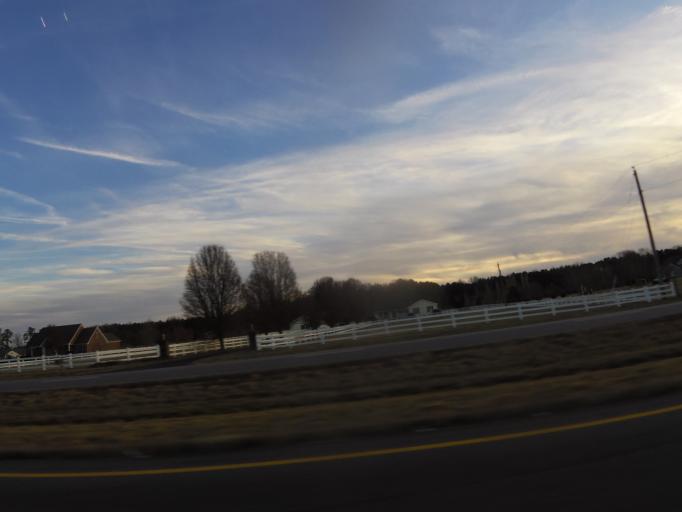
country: US
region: Virginia
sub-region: City of Franklin
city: Franklin
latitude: 36.6905
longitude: -76.9875
